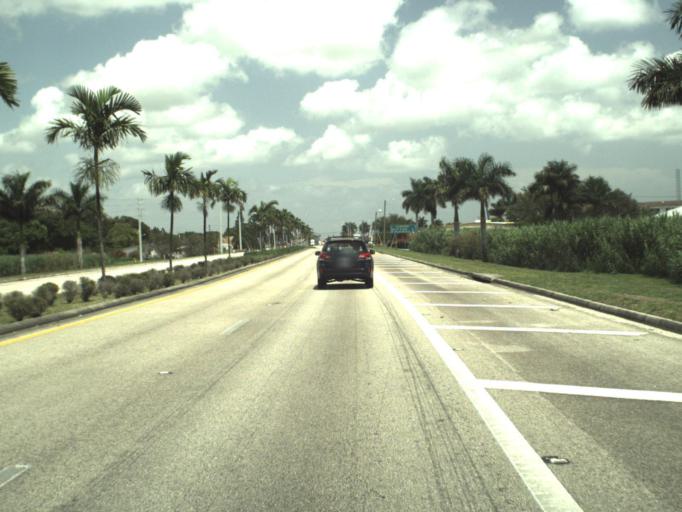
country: US
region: Florida
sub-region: Palm Beach County
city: South Bay
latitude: 26.6589
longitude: -80.7132
